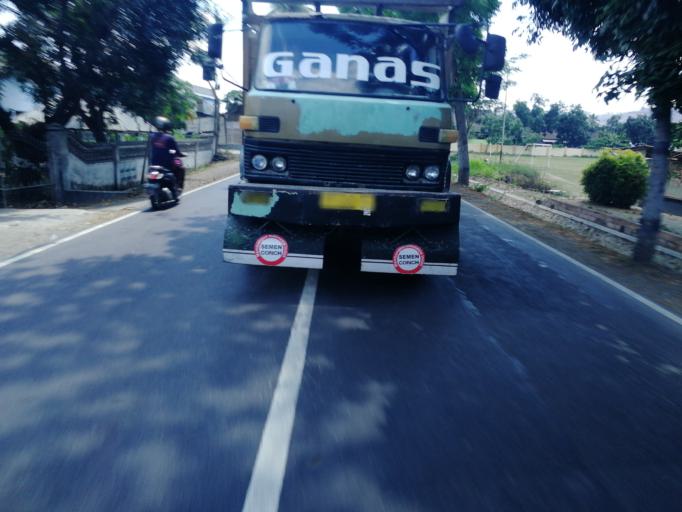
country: ID
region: West Nusa Tenggara
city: Jelateng Timur
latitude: -8.7042
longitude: 116.0903
